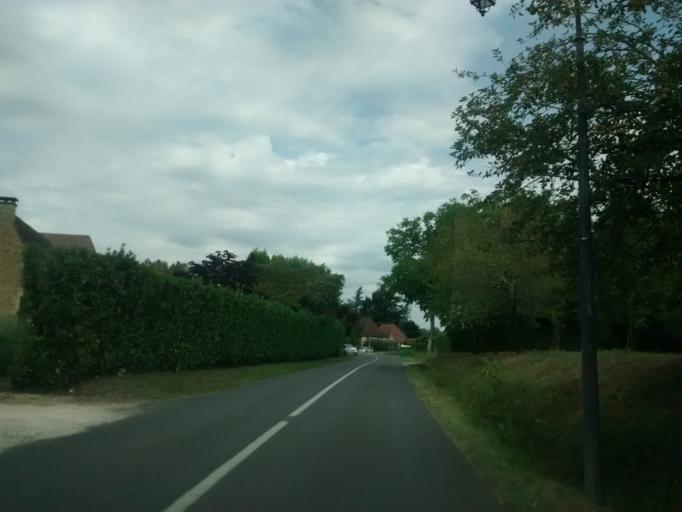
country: FR
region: Aquitaine
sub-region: Departement de la Dordogne
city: Cenac-et-Saint-Julien
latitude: 44.8323
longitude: 1.1636
